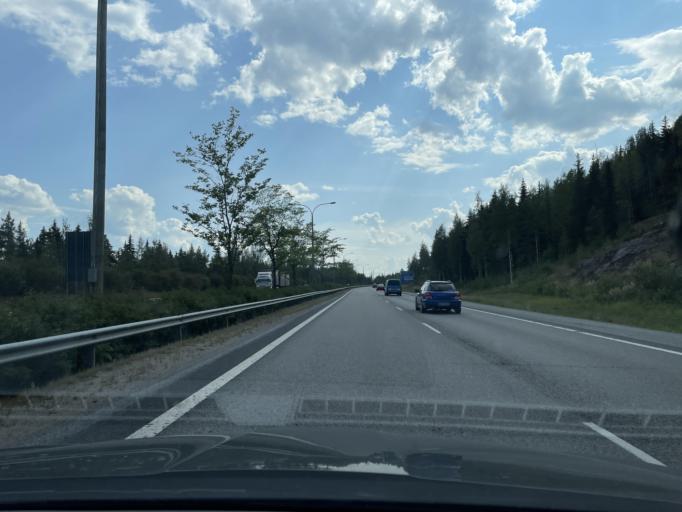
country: FI
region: Central Finland
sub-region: Jyvaeskylae
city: Jyvaeskylae
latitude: 62.2015
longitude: 25.7094
